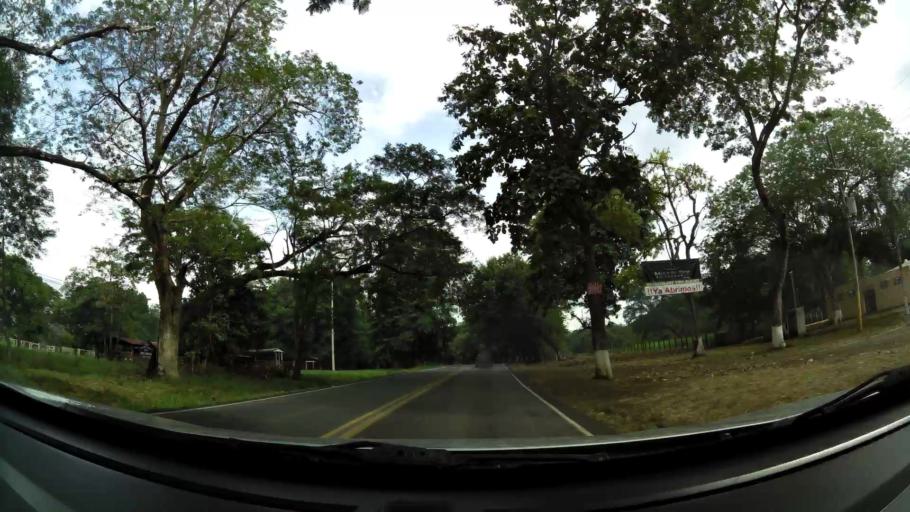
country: CR
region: Guanacaste
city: Juntas
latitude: 10.2446
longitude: -84.9976
